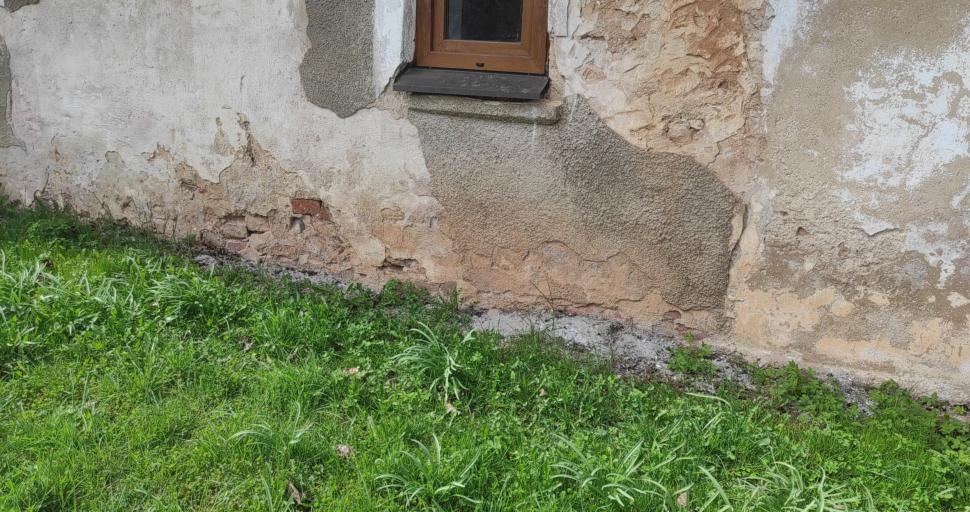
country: LV
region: Talsu Rajons
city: Sabile
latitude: 56.9471
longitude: 22.3514
